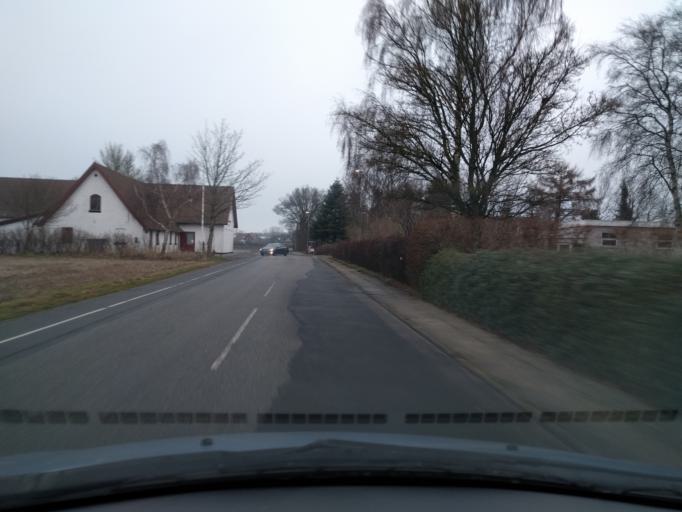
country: DK
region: South Denmark
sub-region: Odense Kommune
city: Bullerup
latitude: 55.4057
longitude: 10.5109
